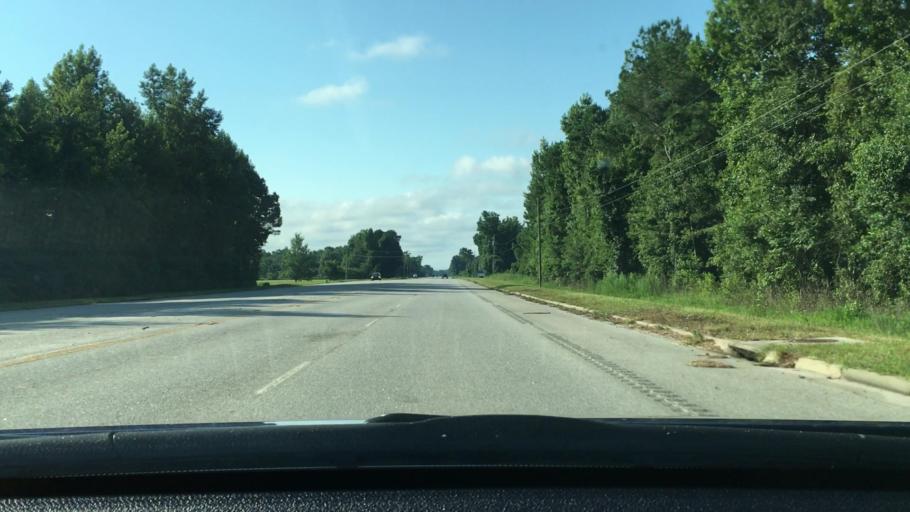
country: US
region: South Carolina
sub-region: Clarendon County
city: Manning
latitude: 33.7695
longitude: -80.2356
